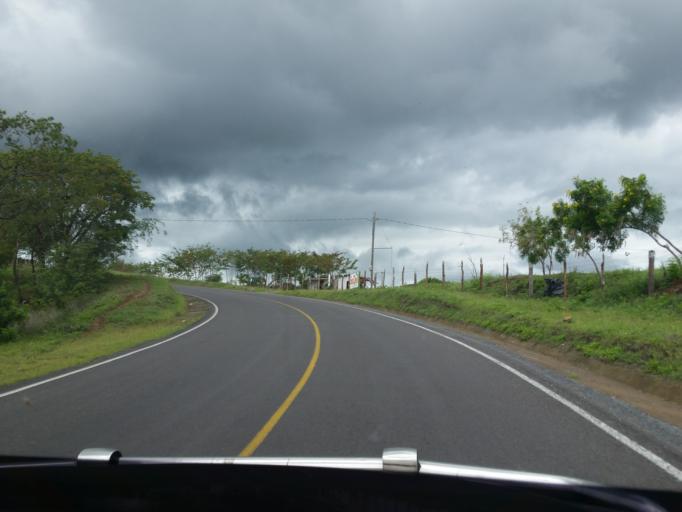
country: NI
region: Matagalpa
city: Matagalpa
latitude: 12.9555
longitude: -86.0267
